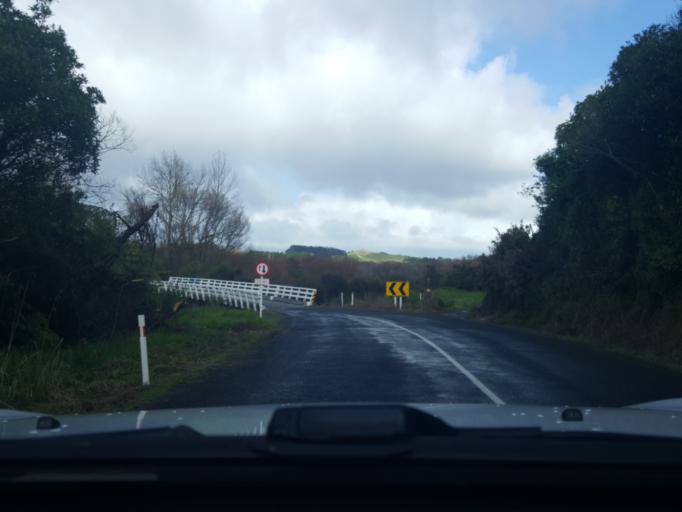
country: NZ
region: Waikato
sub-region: Waikato District
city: Te Kauwhata
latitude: -37.4091
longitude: 175.0589
